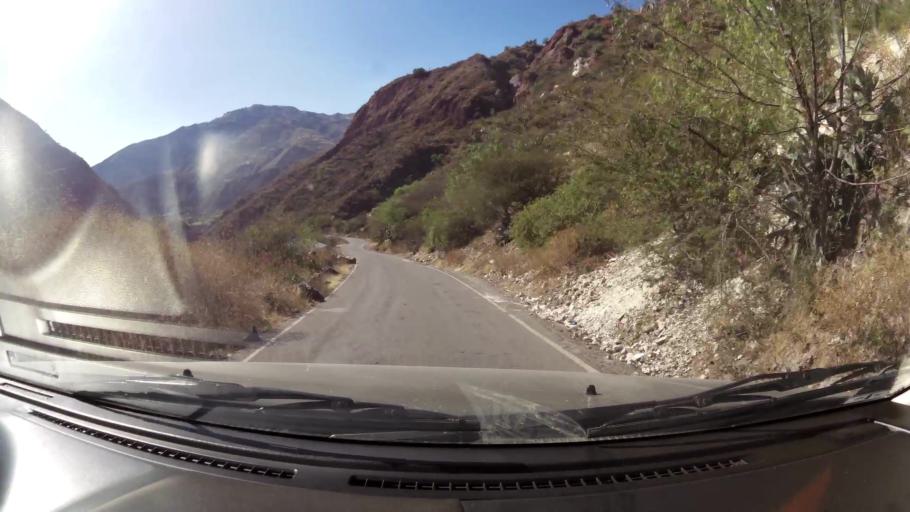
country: PE
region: Huancavelica
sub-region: Provincia de Acobamba
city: Pomacocha
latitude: -12.7799
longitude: -74.4975
